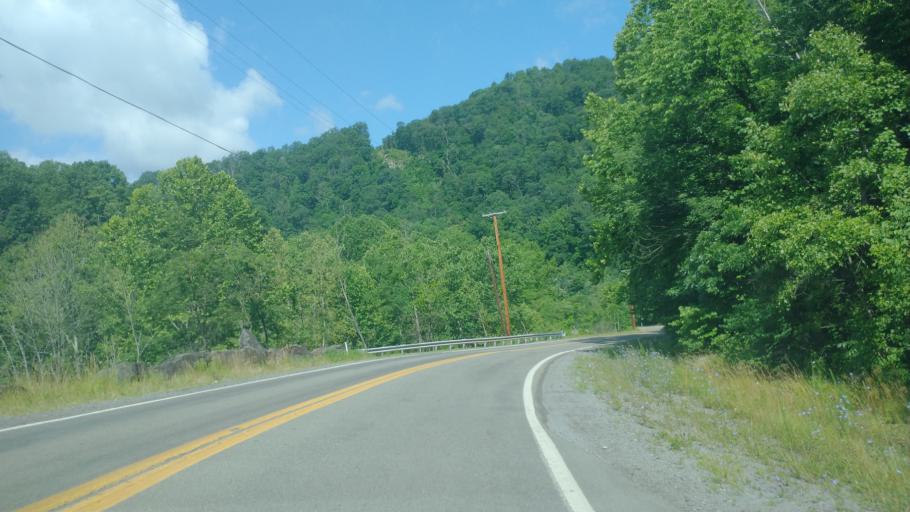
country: US
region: West Virginia
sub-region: McDowell County
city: Welch
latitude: 37.4140
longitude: -81.5234
